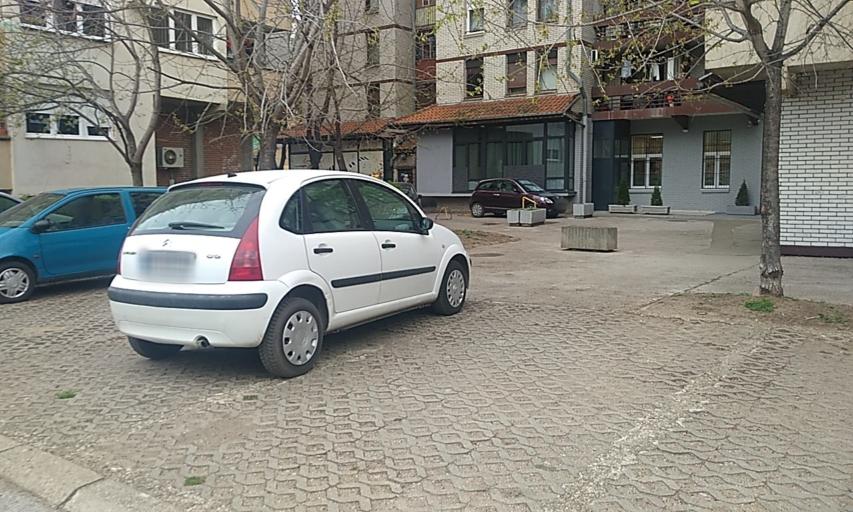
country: RS
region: Central Serbia
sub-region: Nisavski Okrug
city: Nis
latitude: 43.3168
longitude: 21.8991
